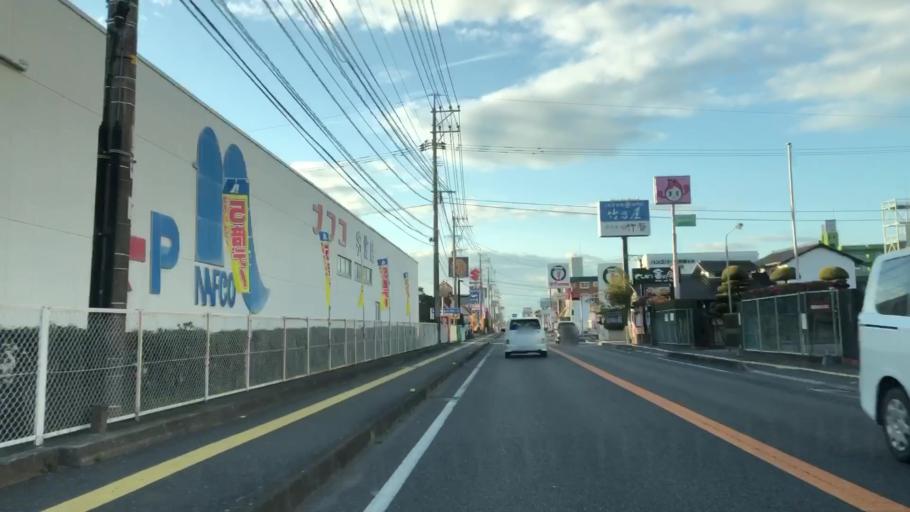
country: JP
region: Oita
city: Bungo-Takada-shi
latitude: 33.5308
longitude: 131.3355
